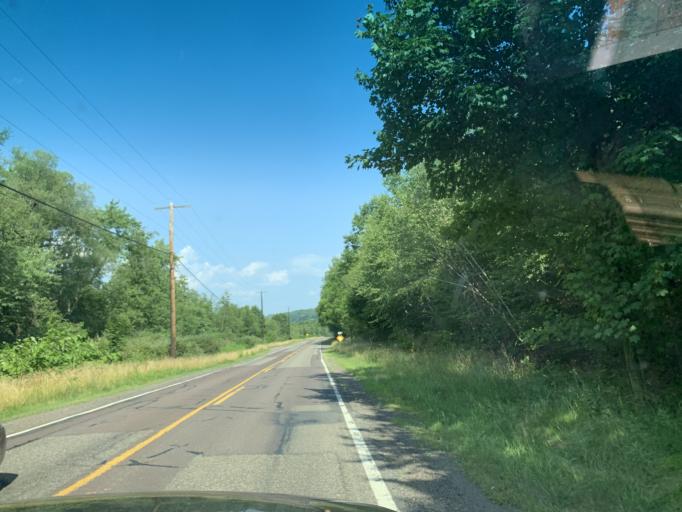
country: US
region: Pennsylvania
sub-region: Schuylkill County
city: Ashland
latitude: 40.8045
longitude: -76.3329
